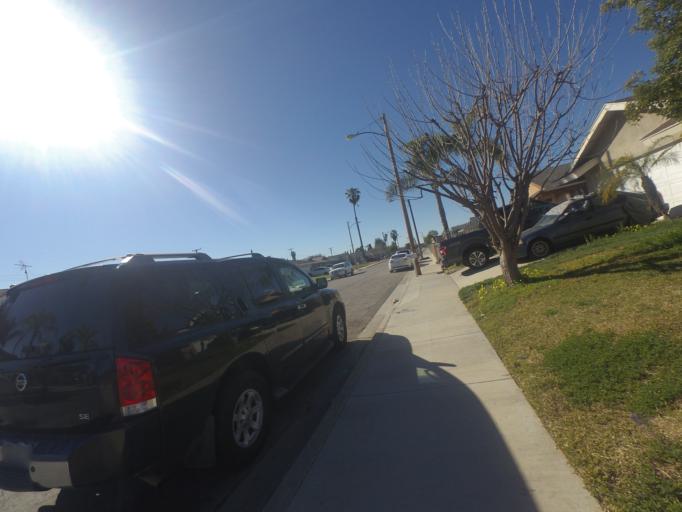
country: US
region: California
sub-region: Riverside County
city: March Air Force Base
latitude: 33.9228
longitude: -117.2692
